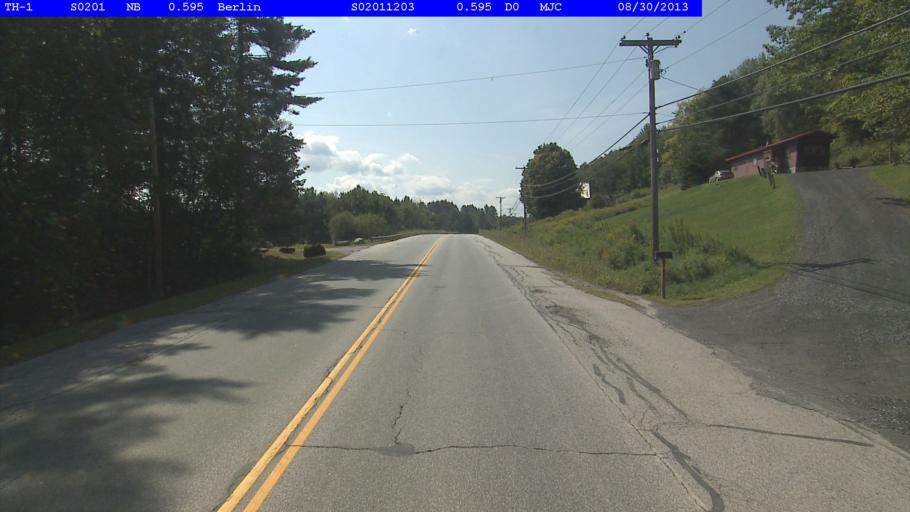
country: US
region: Vermont
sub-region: Washington County
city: Montpelier
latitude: 44.2297
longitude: -72.5638
